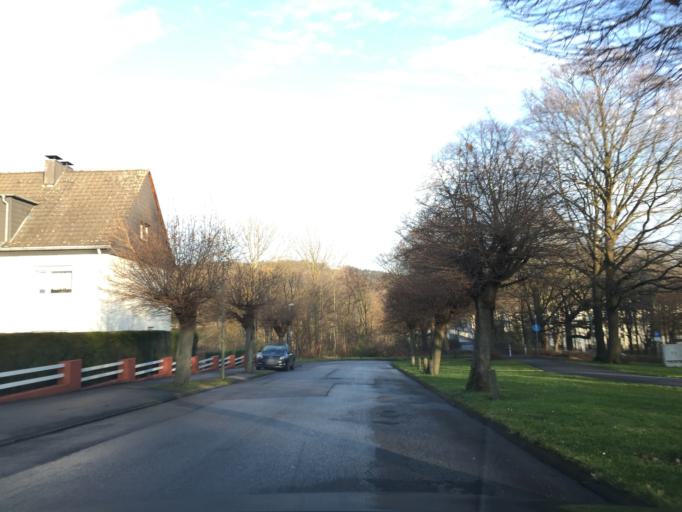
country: DE
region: North Rhine-Westphalia
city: Iserlohn
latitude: 51.3843
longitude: 7.7107
